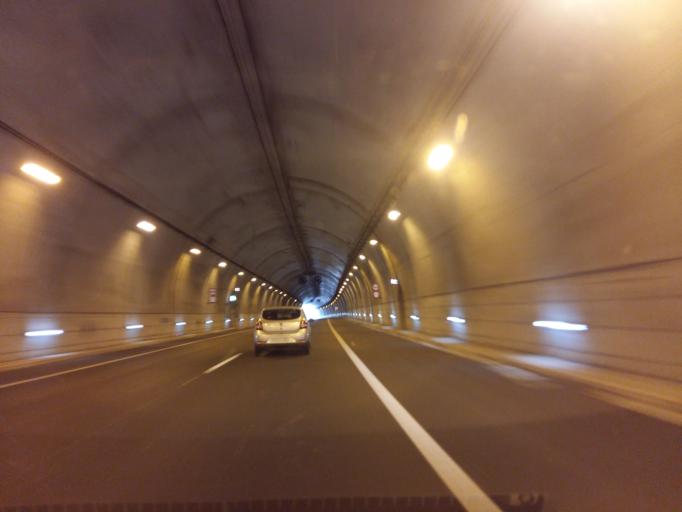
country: ES
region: Cantabria
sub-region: Provincia de Cantabria
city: Camargo
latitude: 43.3967
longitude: -3.8676
